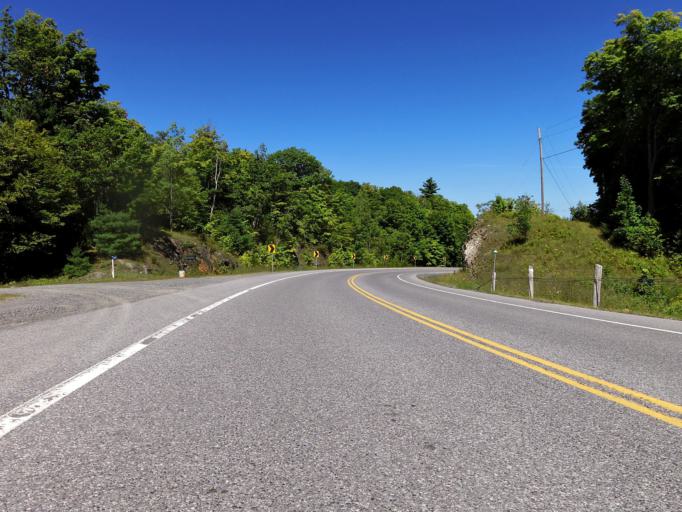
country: CA
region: Ontario
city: Arnprior
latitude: 45.1556
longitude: -76.5185
